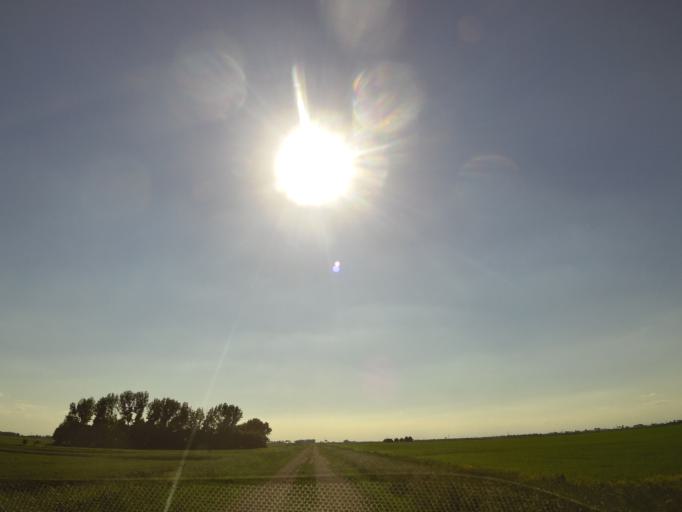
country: US
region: North Dakota
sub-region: Walsh County
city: Grafton
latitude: 48.3979
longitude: -97.2431
